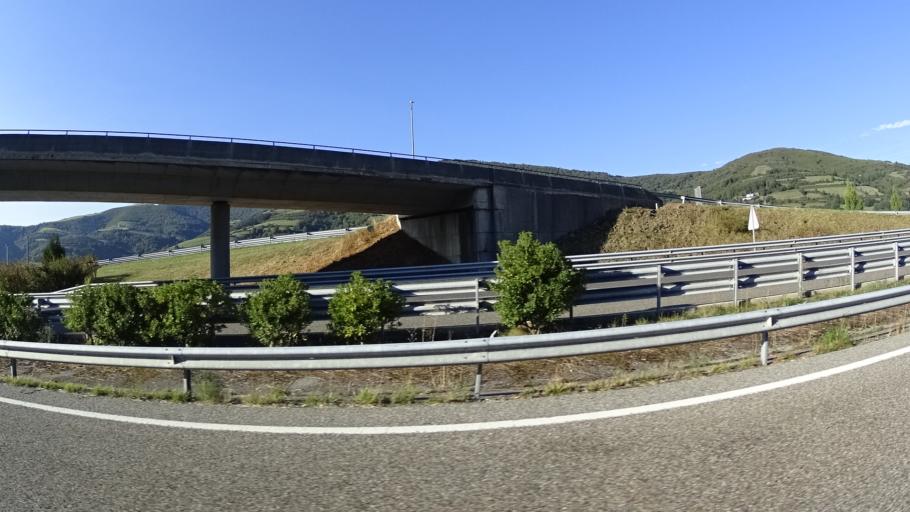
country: ES
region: Galicia
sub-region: Provincia de Lugo
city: San Roman
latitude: 42.7649
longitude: -7.0840
